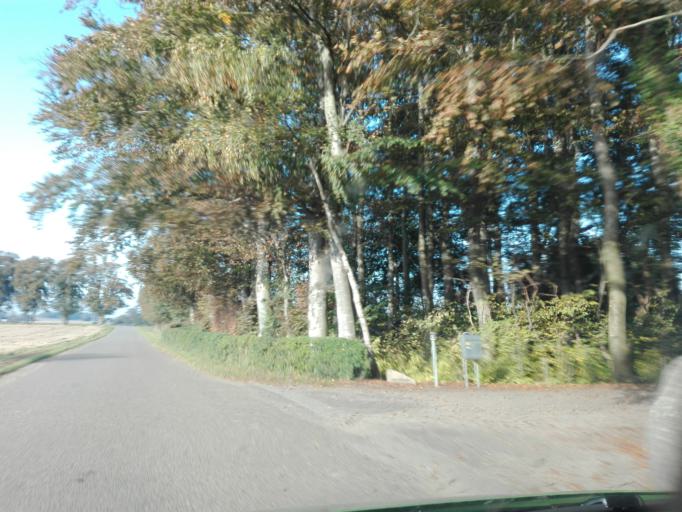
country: DK
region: Central Jutland
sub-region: Odder Kommune
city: Odder
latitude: 55.9184
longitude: 10.1875
